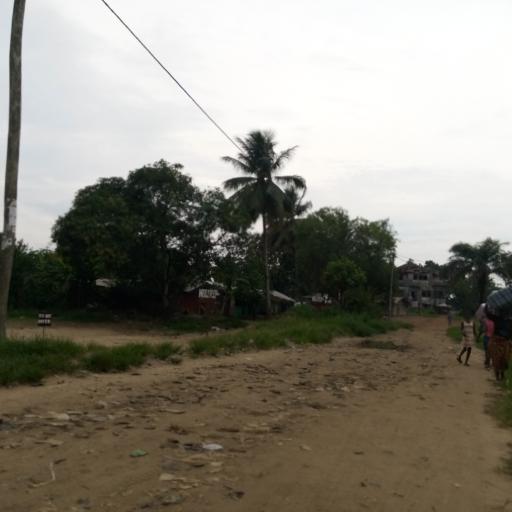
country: LR
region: Montserrado
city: Monrovia
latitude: 6.2979
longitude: -10.6875
